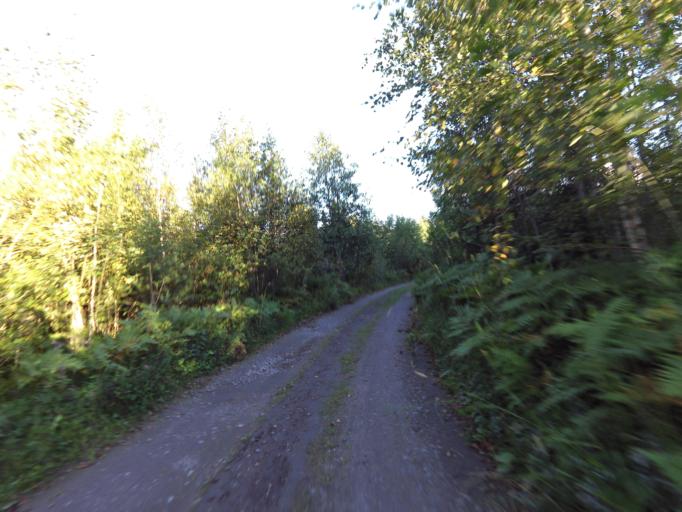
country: SE
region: Gaevleborg
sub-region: Gavle Kommun
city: Gavle
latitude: 60.7209
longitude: 17.1482
